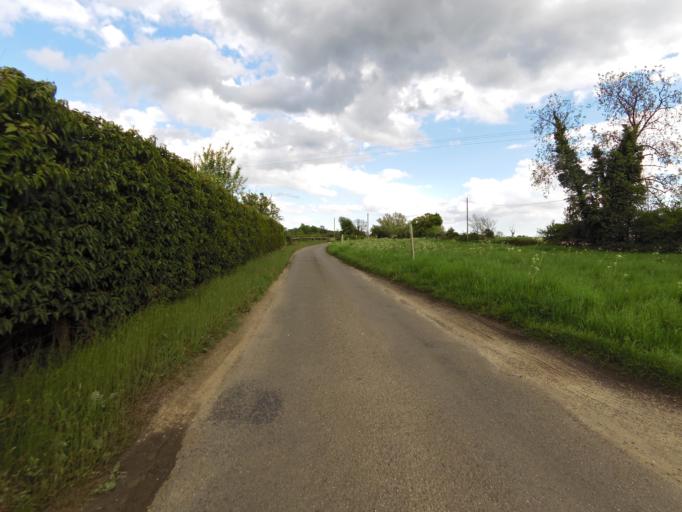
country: GB
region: England
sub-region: Suffolk
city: Elmswell
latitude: 52.2059
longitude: 0.9235
